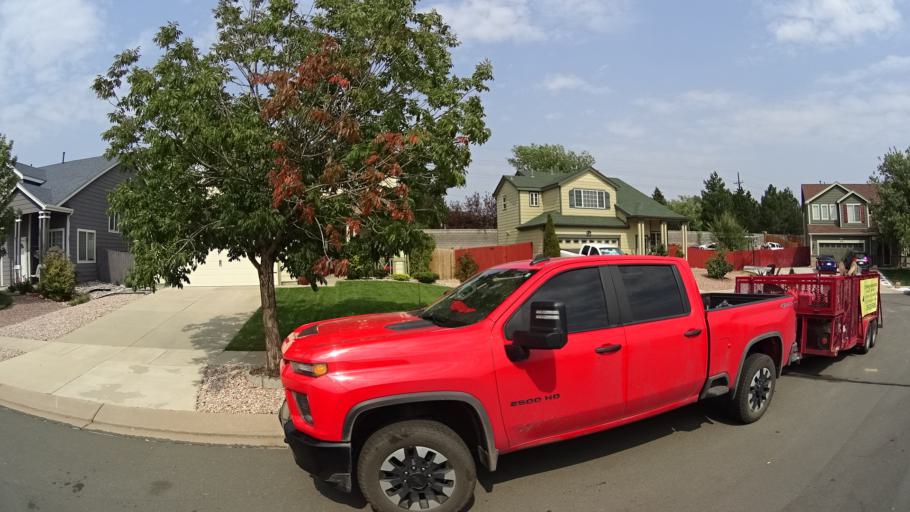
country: US
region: Colorado
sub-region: El Paso County
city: Cimarron Hills
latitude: 38.8245
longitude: -104.7325
